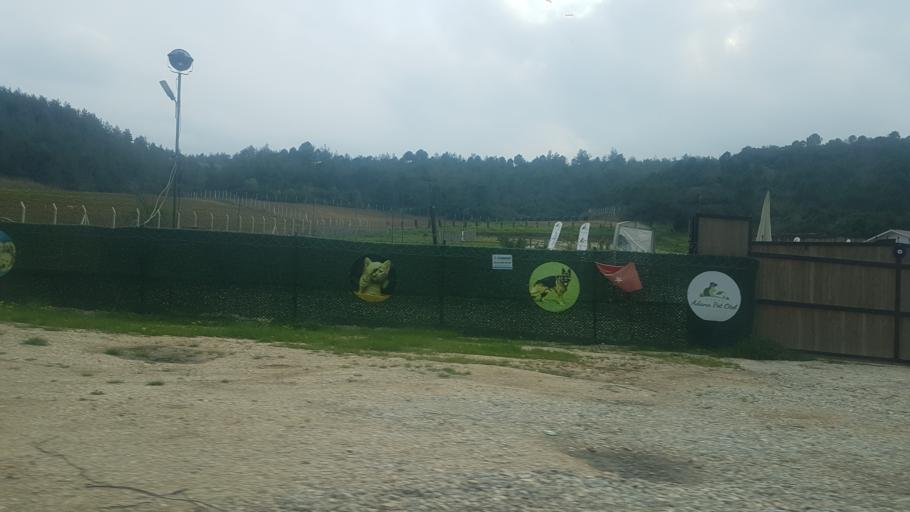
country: TR
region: Mersin
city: Yenice
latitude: 37.0916
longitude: 35.1488
